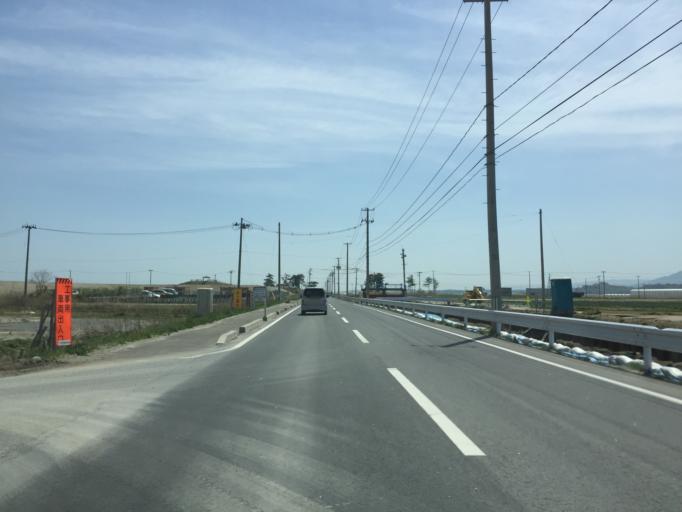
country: JP
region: Miyagi
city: Watari
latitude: 37.9614
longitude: 140.9088
